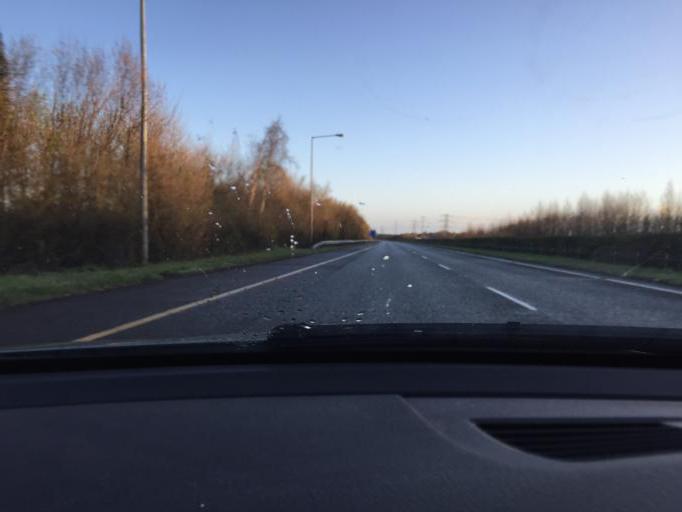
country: IE
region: Leinster
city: Balrothery
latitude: 53.5707
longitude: -6.2122
